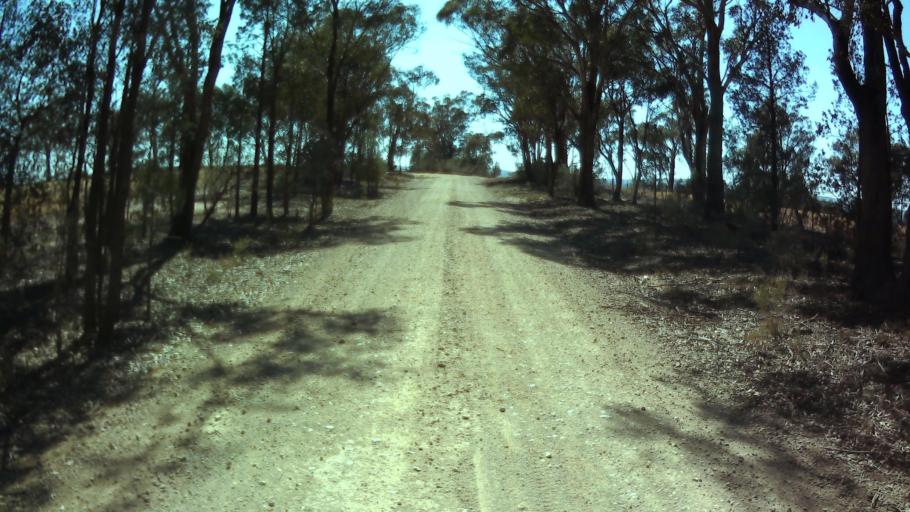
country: AU
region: New South Wales
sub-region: Weddin
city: Grenfell
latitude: -33.9017
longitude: 147.8770
